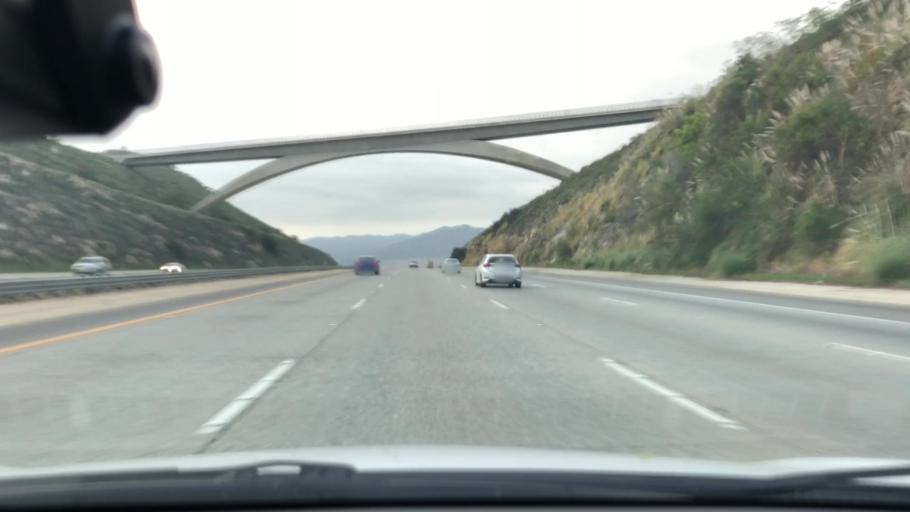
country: US
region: California
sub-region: San Diego County
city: Bonsall
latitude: 33.2976
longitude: -117.1497
